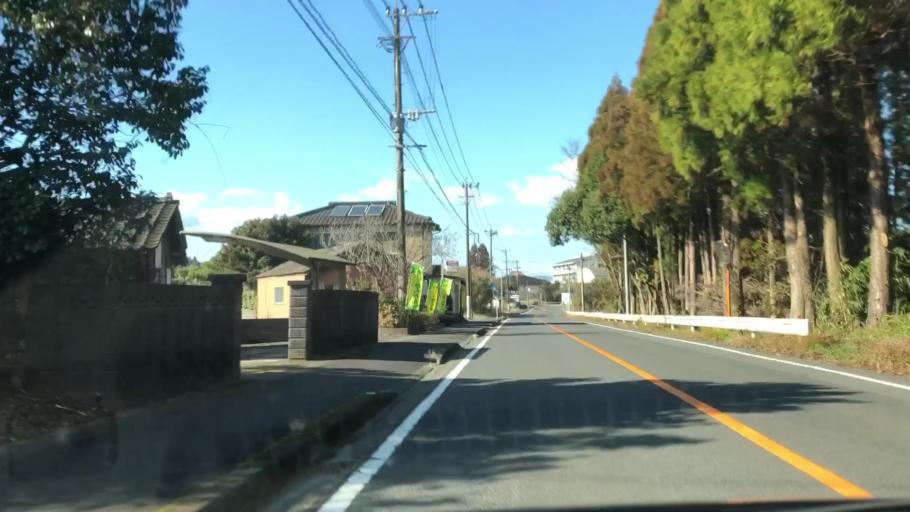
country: JP
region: Kagoshima
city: Satsumasendai
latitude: 31.7993
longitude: 130.4388
